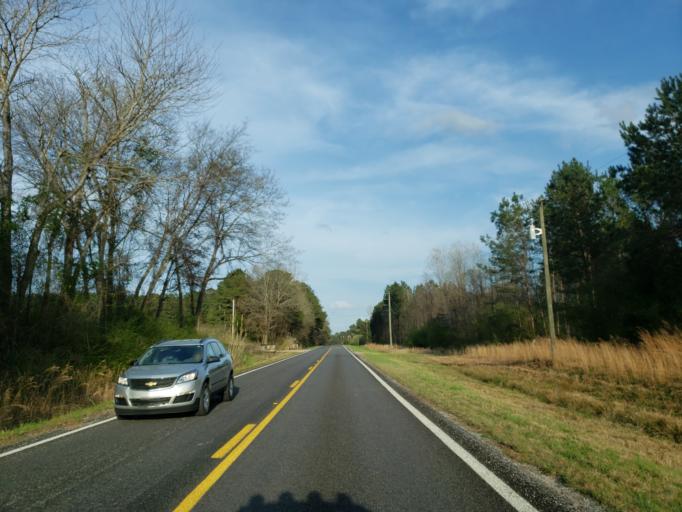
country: US
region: Mississippi
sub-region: Clarke County
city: Stonewall
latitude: 32.1669
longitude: -88.8538
